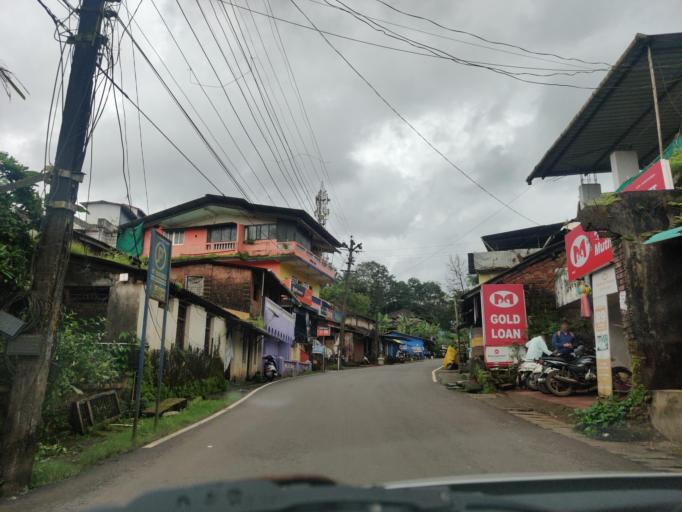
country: IN
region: Goa
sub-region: North Goa
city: Valpoy
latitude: 15.5315
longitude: 74.1376
